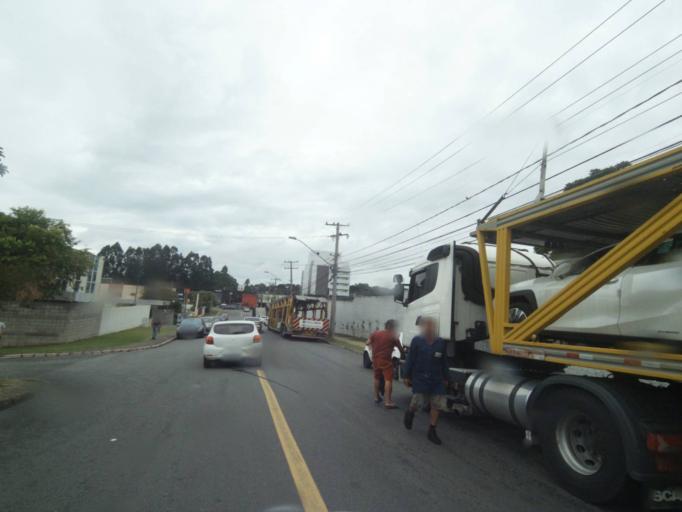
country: BR
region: Parana
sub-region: Curitiba
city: Curitiba
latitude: -25.4347
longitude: -49.3119
